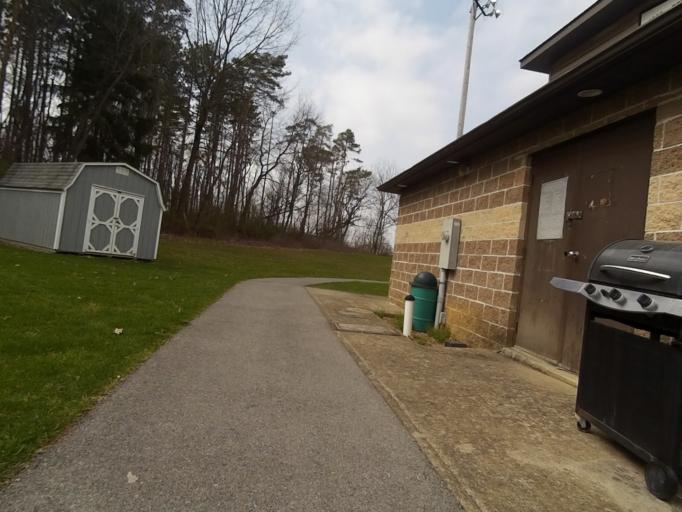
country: US
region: Pennsylvania
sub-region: Centre County
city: Boalsburg
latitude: 40.7861
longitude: -77.8098
